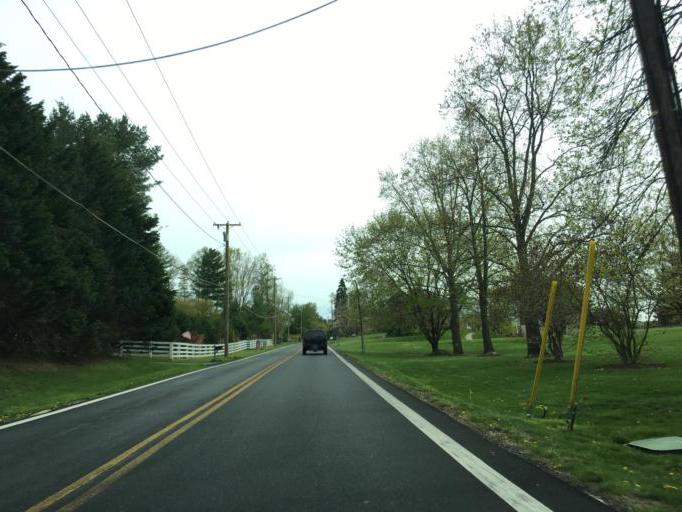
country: US
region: Maryland
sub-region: Baltimore County
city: Hampton
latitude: 39.4930
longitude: -76.5672
